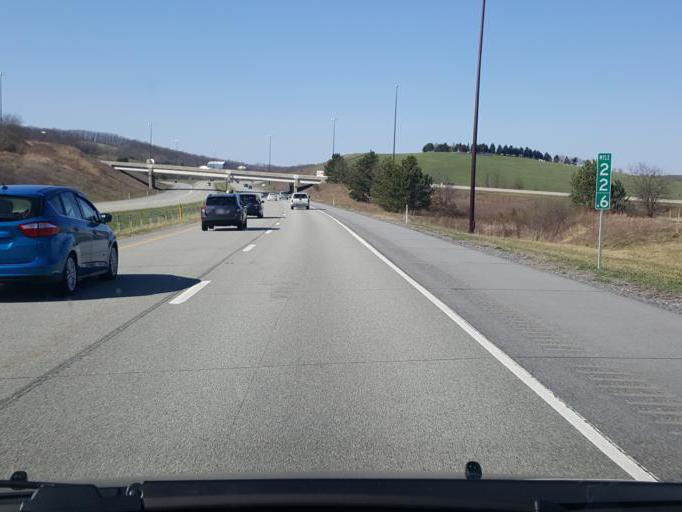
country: US
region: Pennsylvania
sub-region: Blair County
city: Roaring Spring
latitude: 40.3663
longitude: -78.4345
